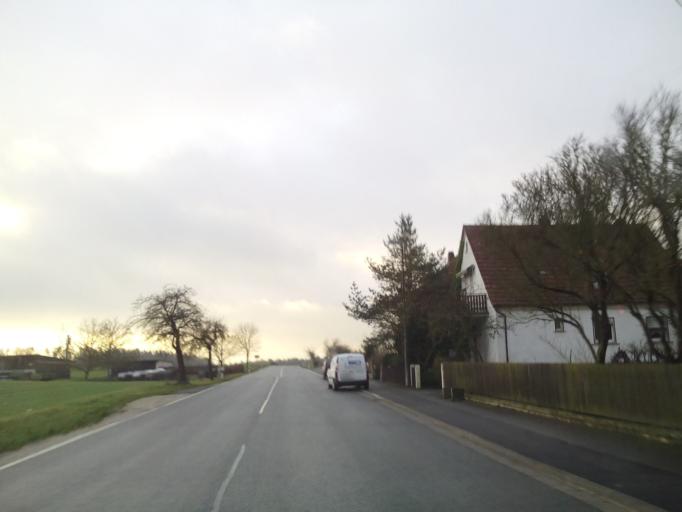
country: DE
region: Bavaria
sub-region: Upper Franconia
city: Untersiemau
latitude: 50.1841
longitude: 11.0167
